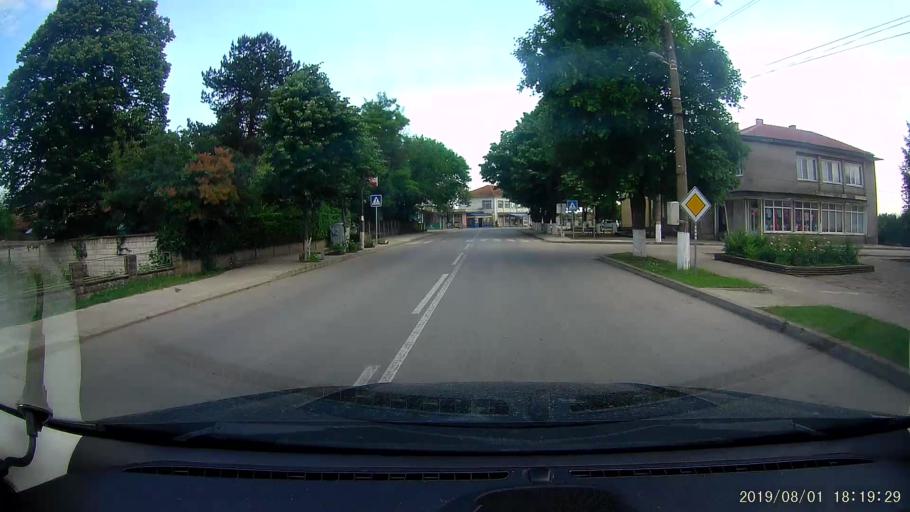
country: BG
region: Shumen
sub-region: Obshtina Kaolinovo
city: Kaolinovo
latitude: 43.6829
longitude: 27.0909
